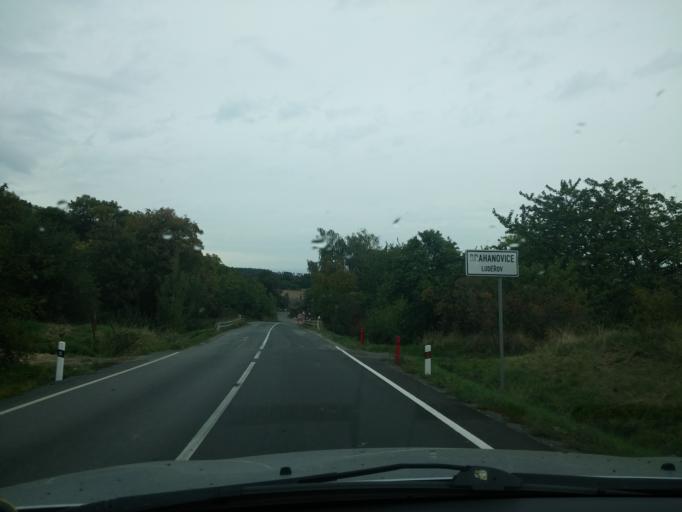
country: CZ
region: Olomoucky
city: Namest' na Hane
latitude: 49.5776
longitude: 17.0439
